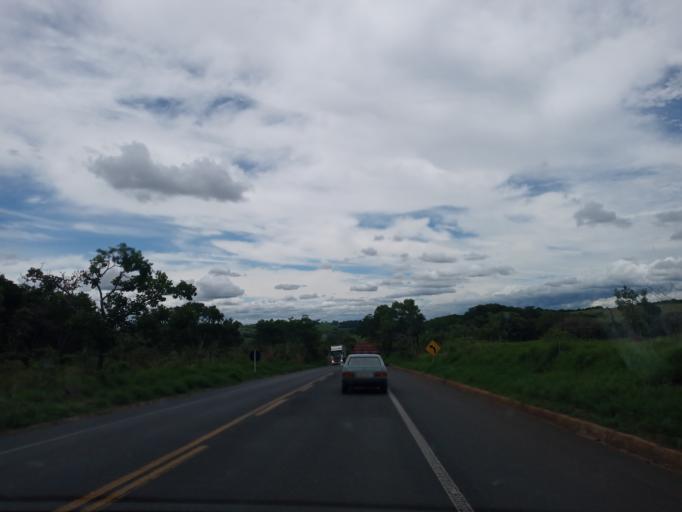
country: BR
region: Minas Gerais
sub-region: Uberlandia
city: Uberlandia
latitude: -19.1660
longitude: -47.9040
